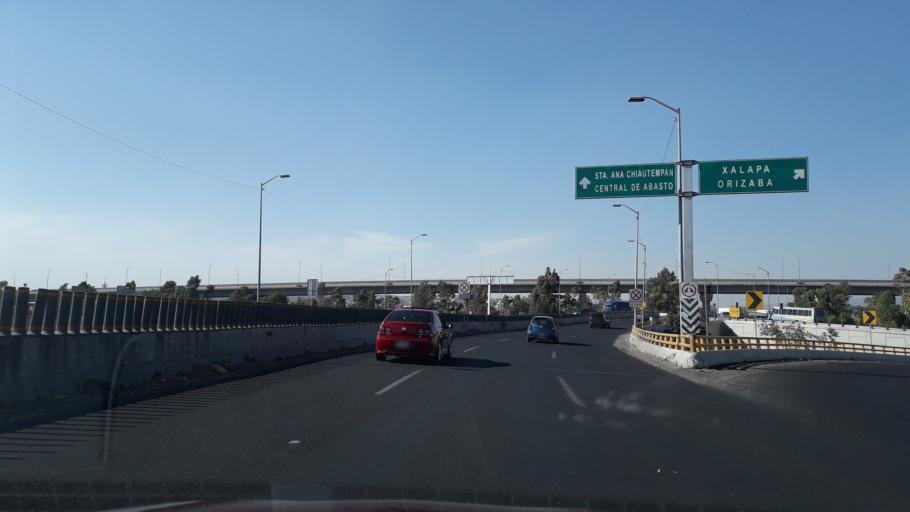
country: MX
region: Puebla
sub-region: Puebla
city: San Sebastian de Aparicio
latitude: 19.0819
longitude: -98.1891
